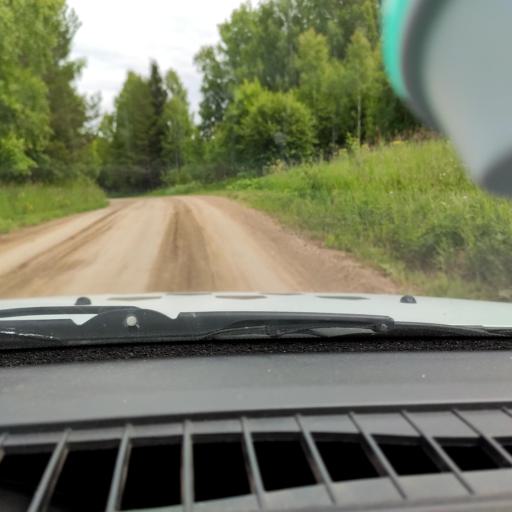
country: RU
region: Perm
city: Suksun
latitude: 57.2040
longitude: 57.6220
